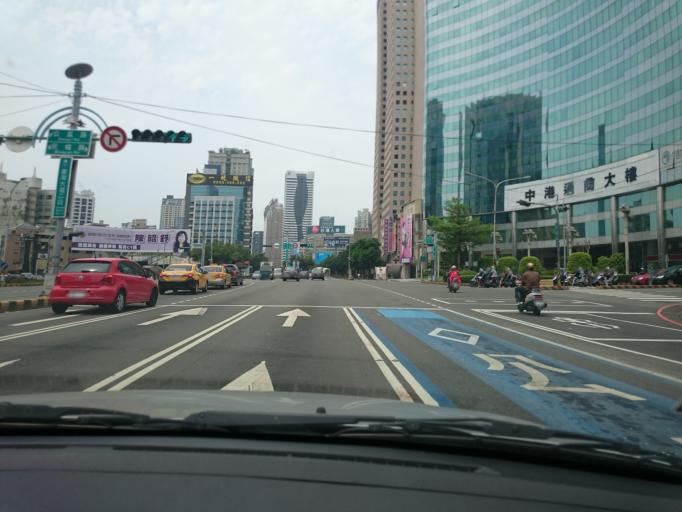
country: TW
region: Taiwan
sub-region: Taichung City
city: Taichung
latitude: 24.1507
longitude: 120.6702
